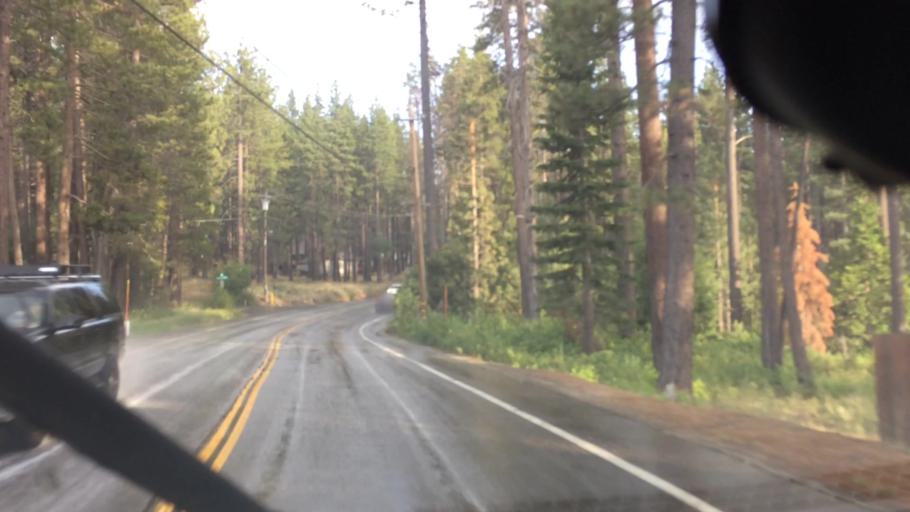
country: US
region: California
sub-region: El Dorado County
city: South Lake Tahoe
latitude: 38.9364
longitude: -119.9540
